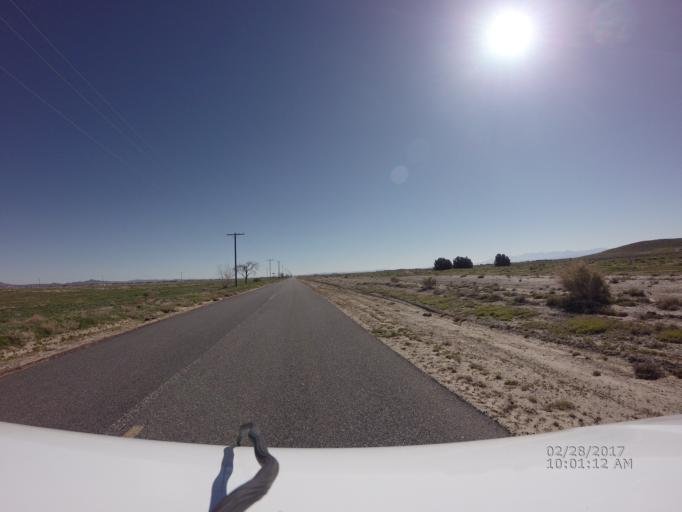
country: US
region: California
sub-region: Kern County
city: Rosamond
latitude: 34.8055
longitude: -118.3055
